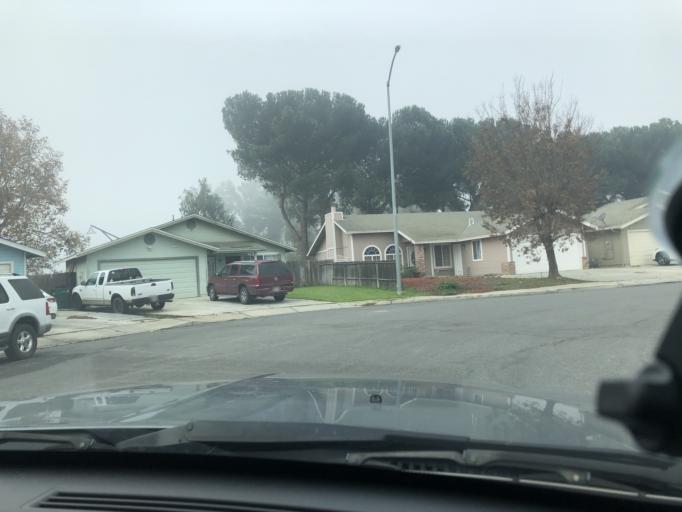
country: US
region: California
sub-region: Monterey County
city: King City
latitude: 36.2045
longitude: -121.1439
